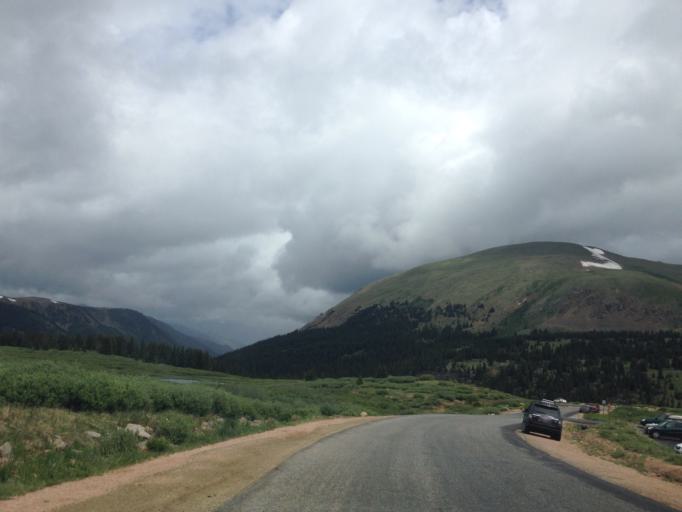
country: US
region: Colorado
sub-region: Clear Creek County
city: Georgetown
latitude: 39.5965
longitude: -105.7107
